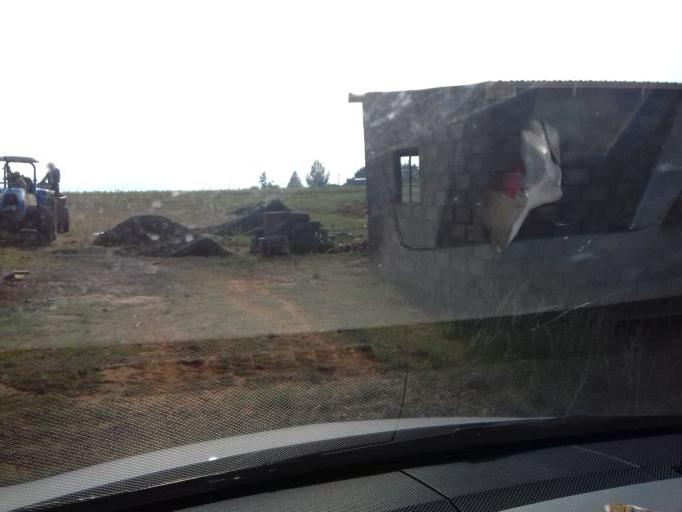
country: LS
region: Maseru
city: Maseru
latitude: -29.4291
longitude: 27.5685
